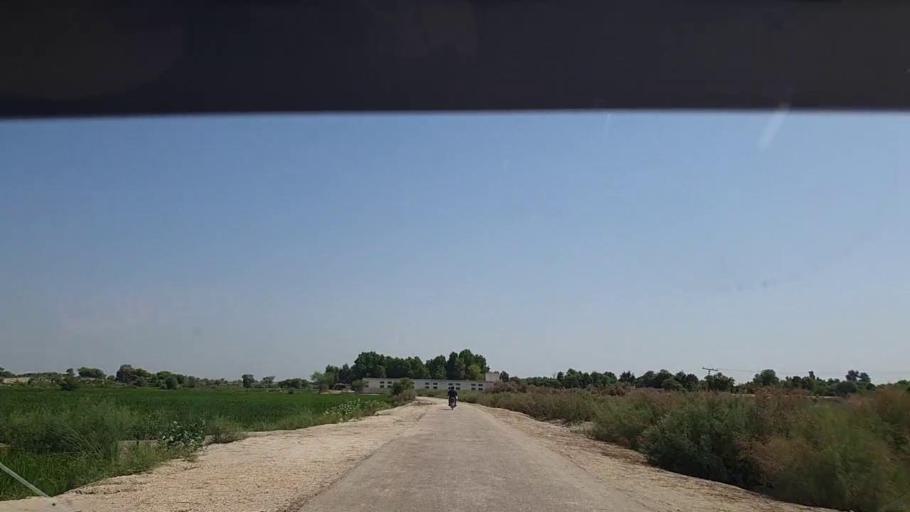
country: PK
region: Sindh
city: Kandhkot
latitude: 28.1659
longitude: 69.1607
